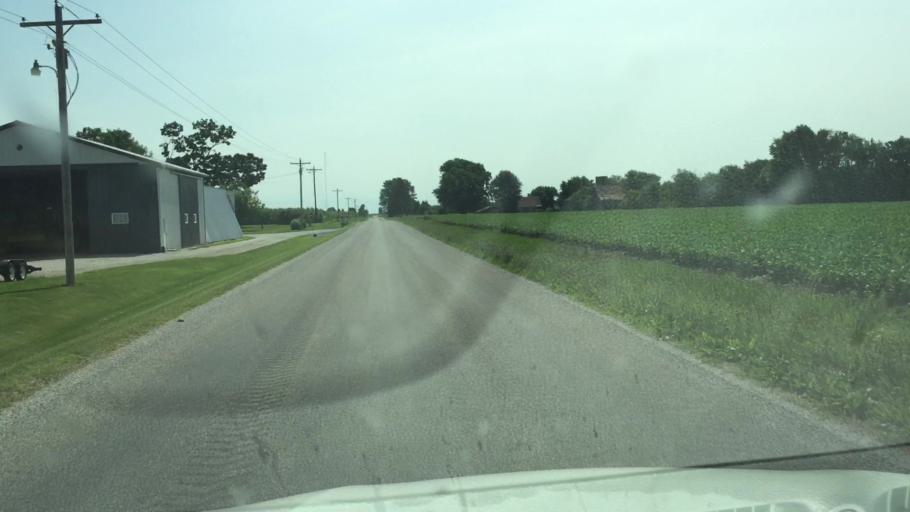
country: US
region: Illinois
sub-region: Hancock County
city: Nauvoo
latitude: 40.5113
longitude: -91.3413
